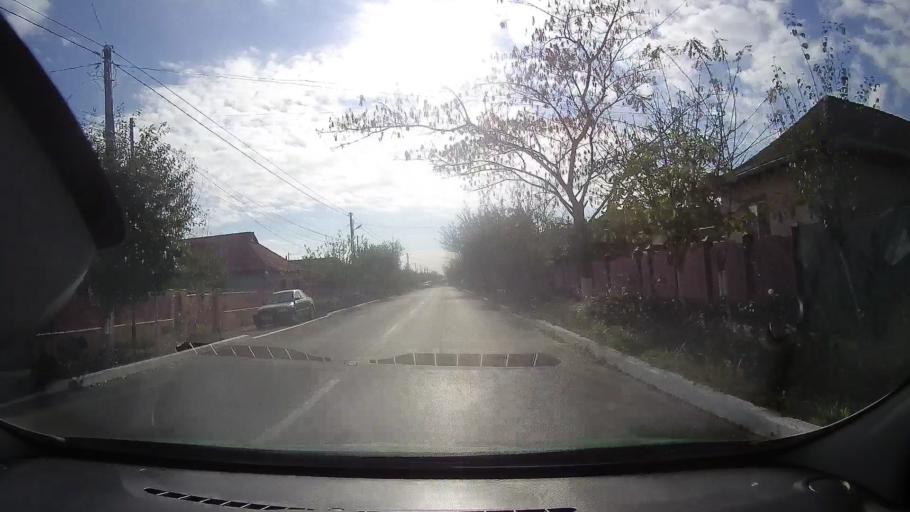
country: RO
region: Tulcea
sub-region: Comuna Sarichioi
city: Sarichioi
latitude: 44.9494
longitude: 28.8517
